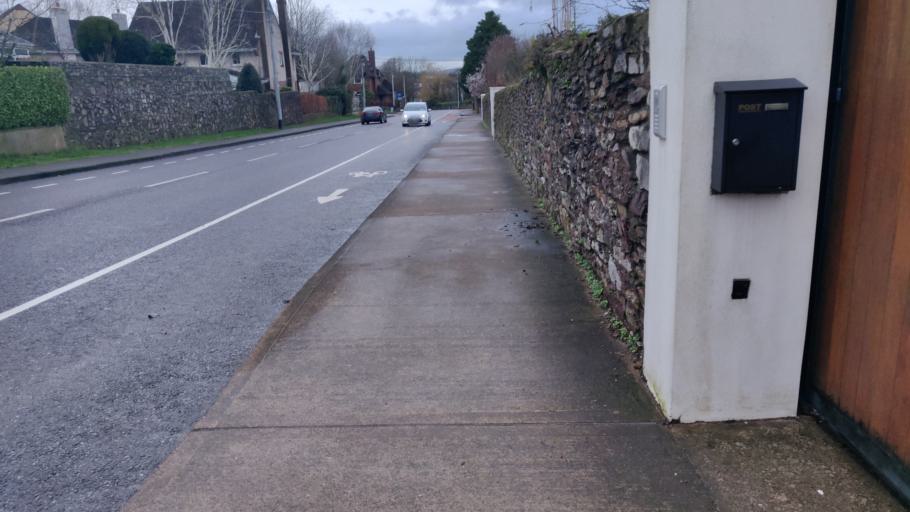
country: IE
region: Munster
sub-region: County Cork
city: Cork
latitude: 51.8750
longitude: -8.4267
